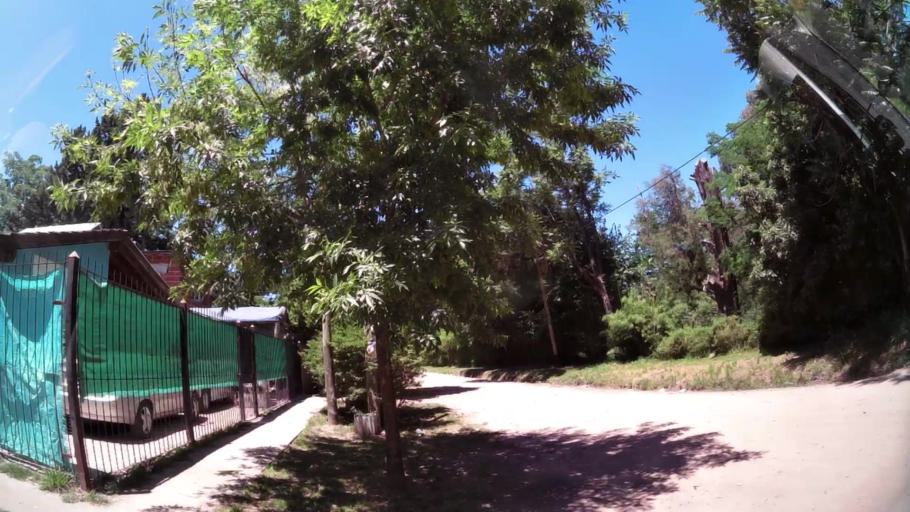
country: AR
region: Buenos Aires
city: Hurlingham
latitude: -34.5074
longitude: -58.7162
